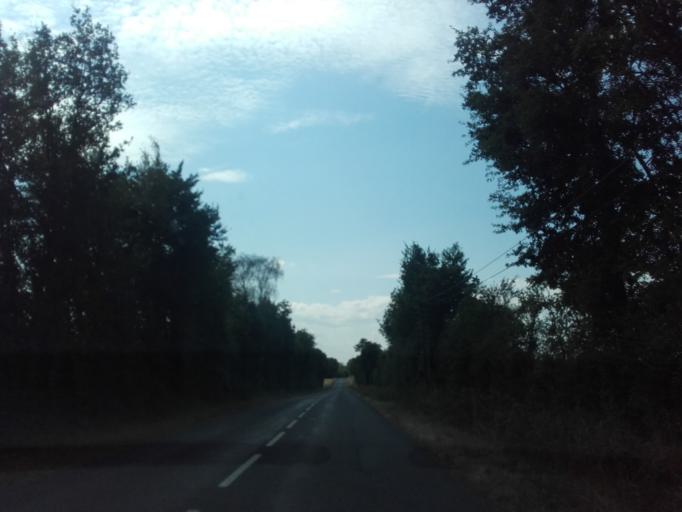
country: FR
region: Rhone-Alpes
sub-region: Departement de l'Ain
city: Chatillon-sur-Chalaronne
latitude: 46.0946
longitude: 5.0075
